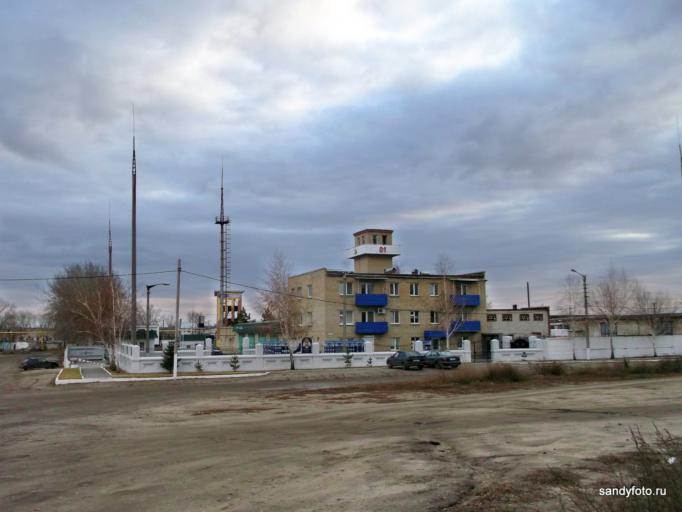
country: RU
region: Chelyabinsk
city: Troitsk
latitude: 54.0755
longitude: 61.5402
